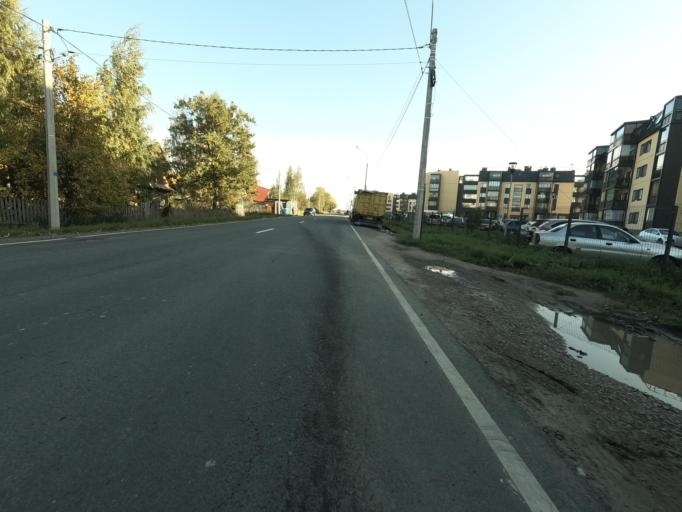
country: RU
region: St.-Petersburg
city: Pontonnyy
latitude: 59.7585
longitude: 30.6270
